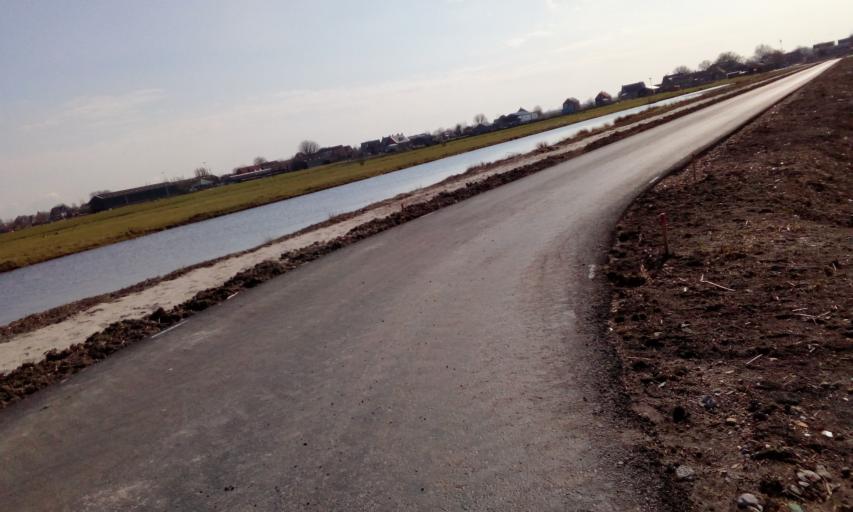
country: NL
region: South Holland
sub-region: Gemeente Pijnacker-Nootdorp
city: Pijnacker
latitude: 51.9903
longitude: 4.4186
